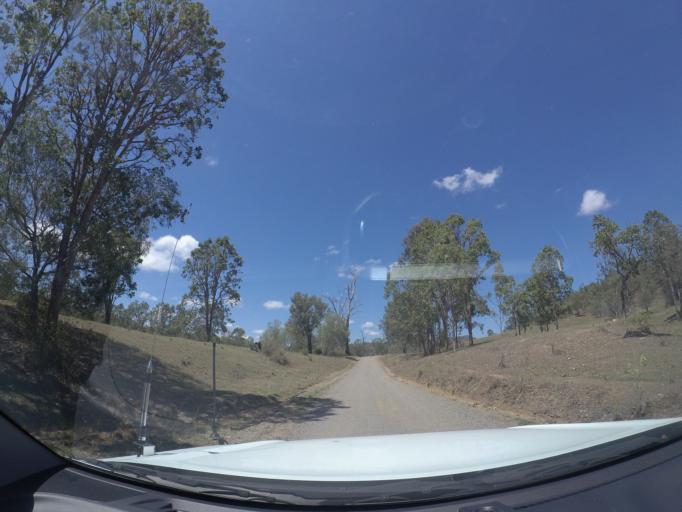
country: AU
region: Queensland
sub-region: Logan
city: Cedar Vale
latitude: -27.8605
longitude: 152.8545
